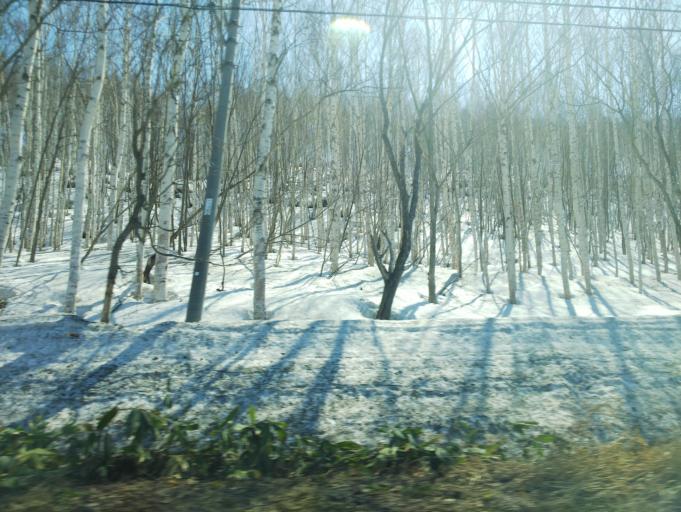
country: JP
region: Hokkaido
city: Nayoro
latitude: 44.6977
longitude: 142.2719
